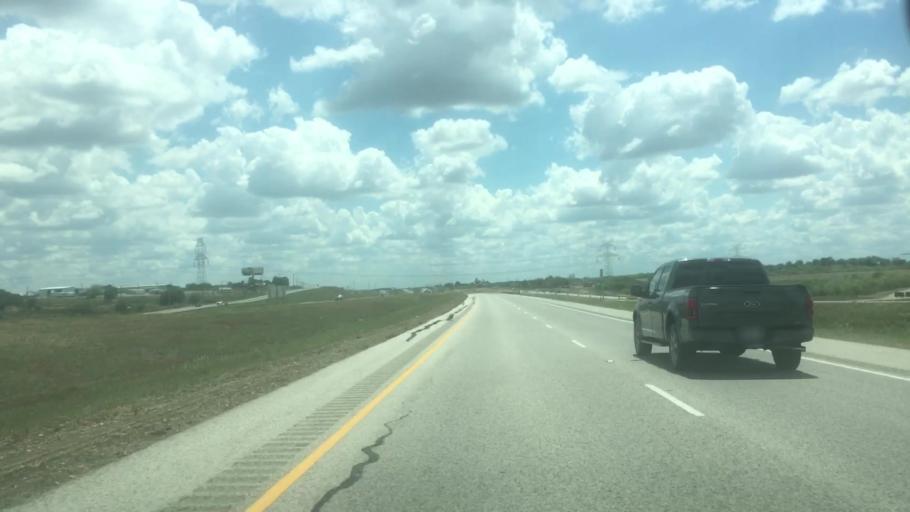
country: US
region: Texas
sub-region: Caldwell County
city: Uhland
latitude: 30.0003
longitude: -97.6868
